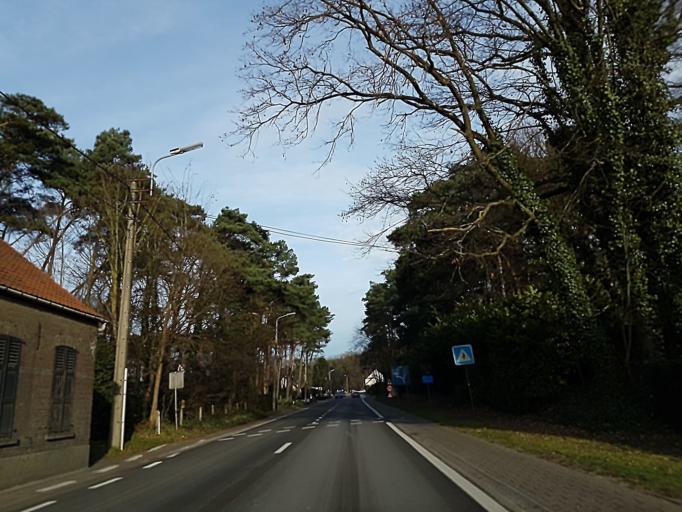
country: BE
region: Flanders
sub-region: Provincie Vlaams-Brabant
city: Haacht
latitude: 50.9907
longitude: 4.6455
